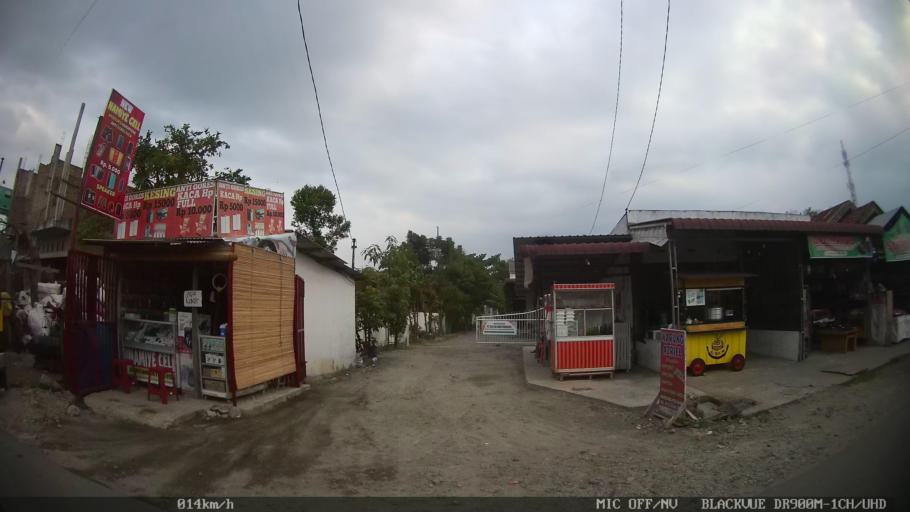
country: ID
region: North Sumatra
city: Sunggal
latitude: 3.5579
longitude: 98.5521
